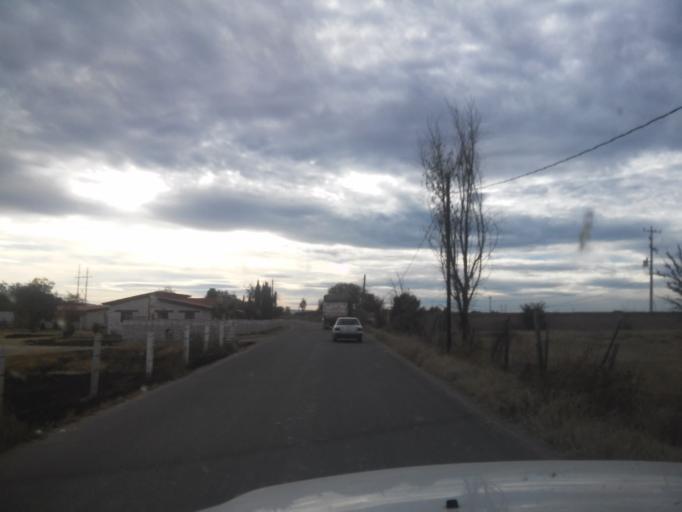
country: MX
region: Durango
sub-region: Durango
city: Jose Refugio Salcido
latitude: 24.0301
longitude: -104.5703
